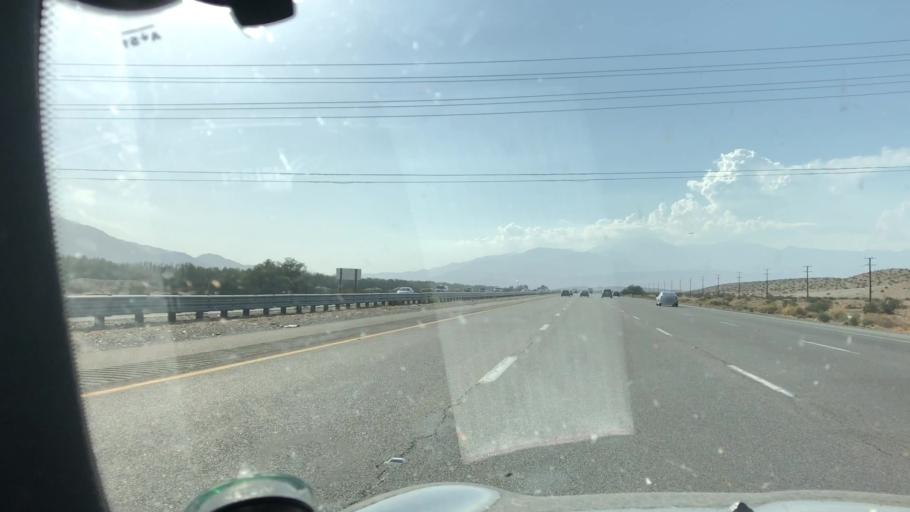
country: US
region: California
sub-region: Riverside County
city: Desert Edge
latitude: 33.8592
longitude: -116.4748
